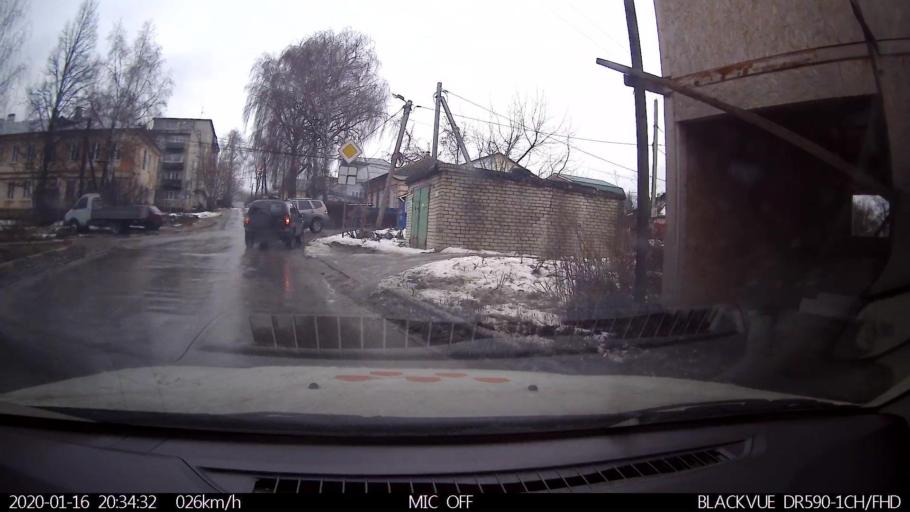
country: RU
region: Nizjnij Novgorod
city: Nizhniy Novgorod
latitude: 56.3124
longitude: 44.0504
